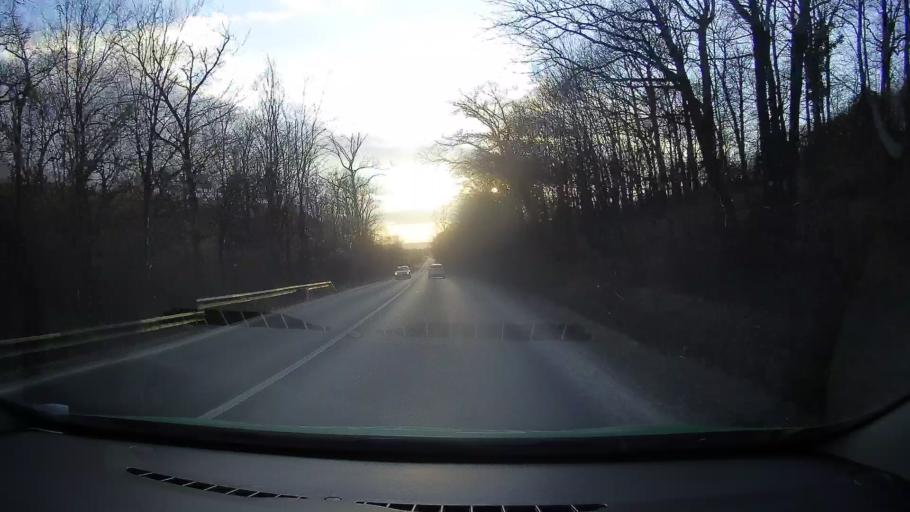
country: RO
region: Dambovita
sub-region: Comuna Gura Ocnitei
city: Adanca
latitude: 44.9106
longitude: 25.6345
